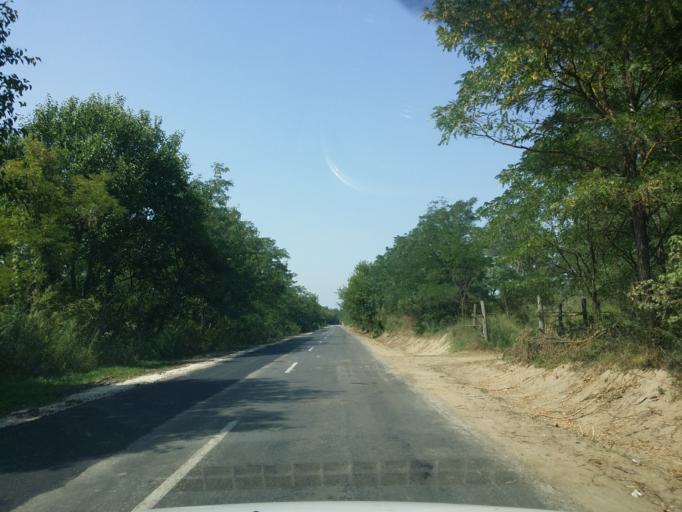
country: HU
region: Tolna
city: Pincehely
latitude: 46.6186
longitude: 18.4185
